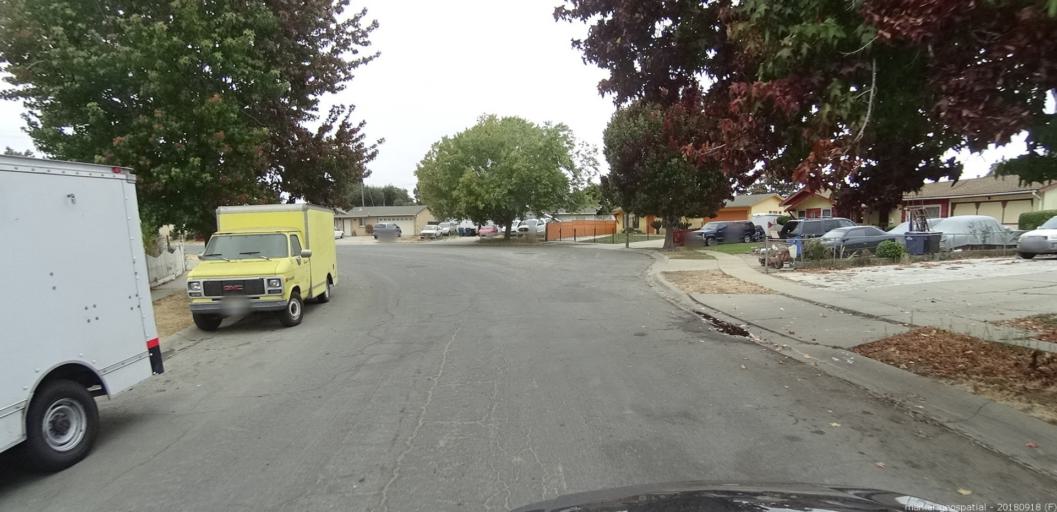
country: US
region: California
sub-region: Monterey County
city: Boronda
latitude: 36.7314
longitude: -121.6336
